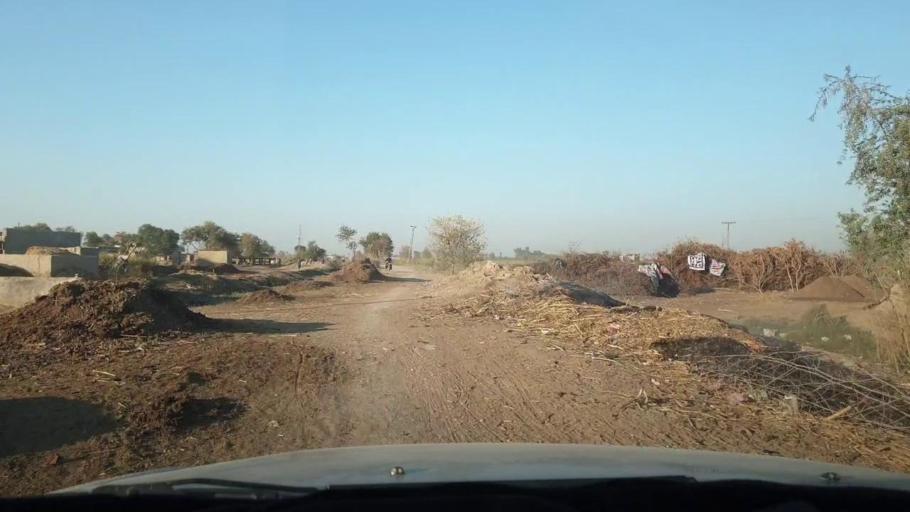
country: PK
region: Sindh
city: Ghotki
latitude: 27.9862
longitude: 69.2730
